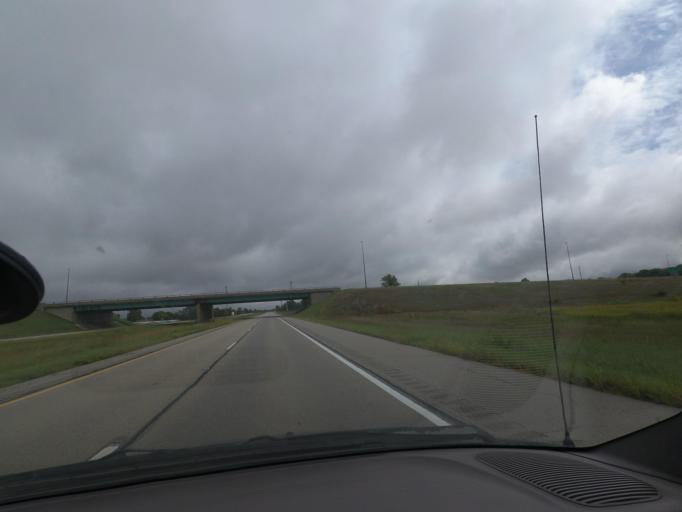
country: US
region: Illinois
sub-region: Piatt County
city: Monticello
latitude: 40.0353
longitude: -88.5973
